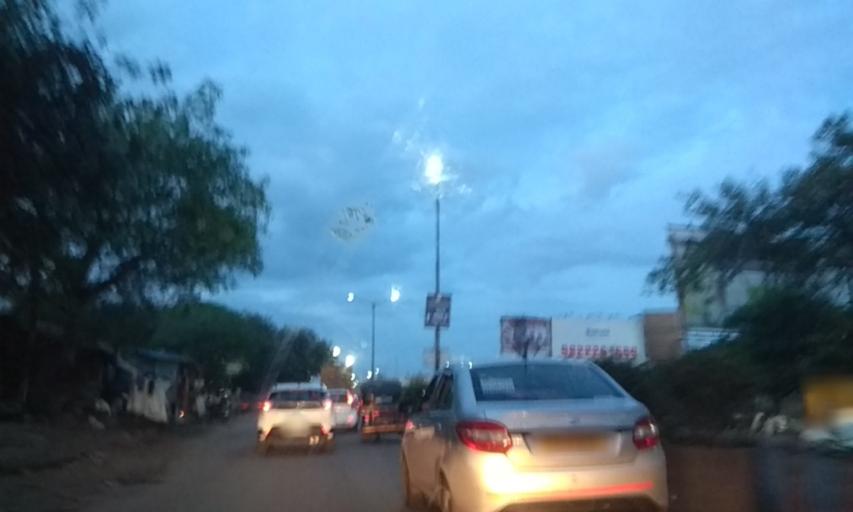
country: IN
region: Maharashtra
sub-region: Pune Division
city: Lohogaon
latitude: 18.5340
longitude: 73.9336
